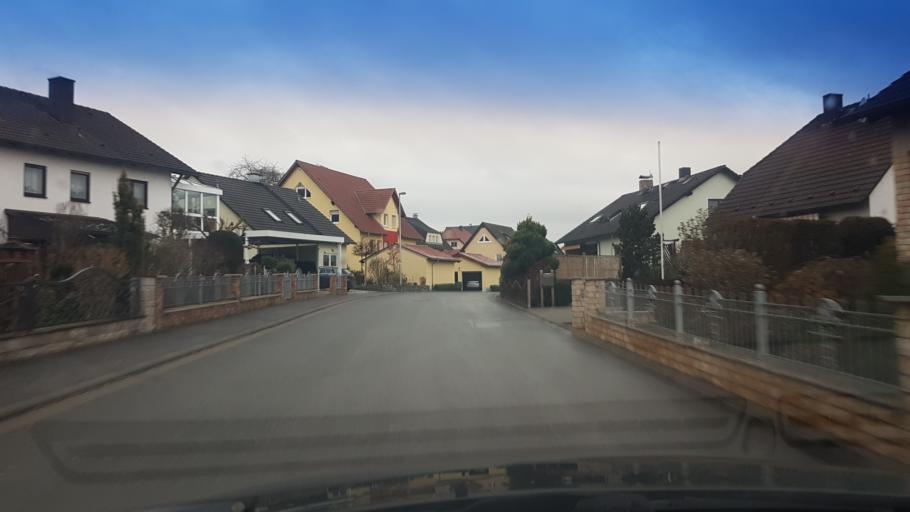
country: DE
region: Bavaria
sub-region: Upper Franconia
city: Hirschaid
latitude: 49.8088
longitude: 10.9758
